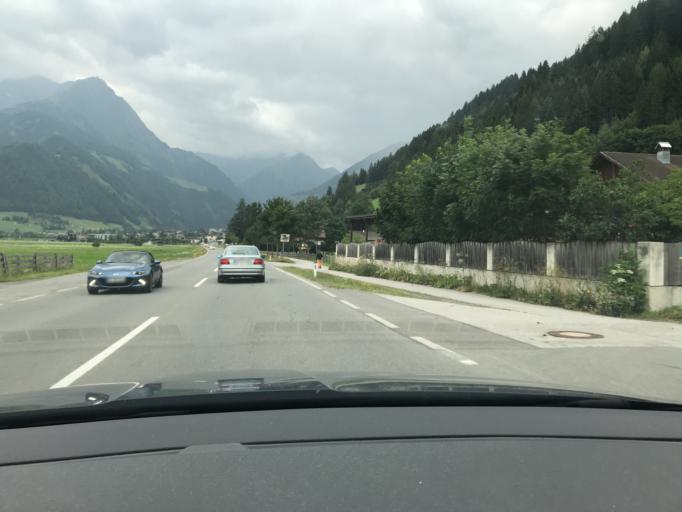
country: AT
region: Tyrol
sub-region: Politischer Bezirk Lienz
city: Matrei in Osttirol
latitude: 46.9848
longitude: 12.5489
